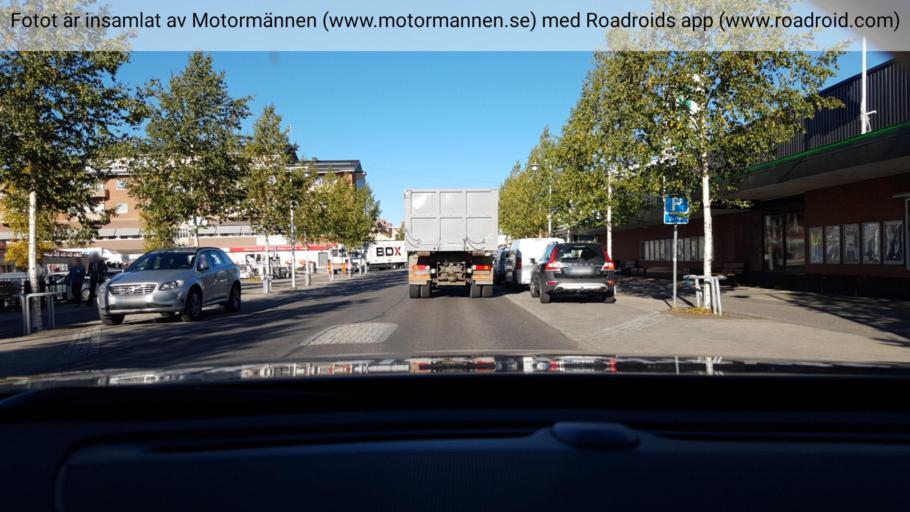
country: SE
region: Norrbotten
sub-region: Arvidsjaurs Kommun
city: Arvidsjaur
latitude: 65.5920
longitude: 19.1780
